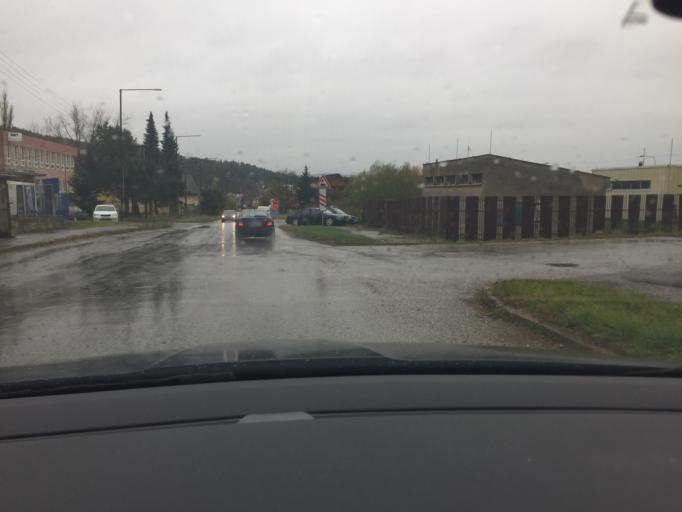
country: SK
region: Presovsky
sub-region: Okres Presov
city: Kezmarok
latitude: 49.1519
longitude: 20.4272
